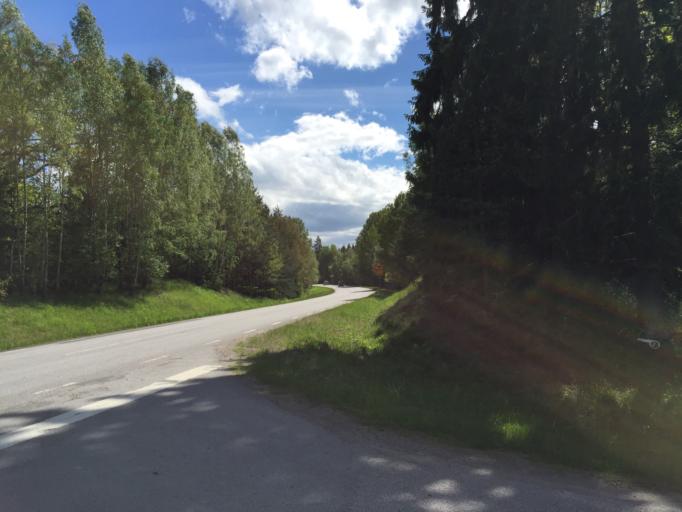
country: SE
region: OEstergoetland
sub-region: Finspangs Kommun
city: Finspang
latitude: 58.6183
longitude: 15.8120
